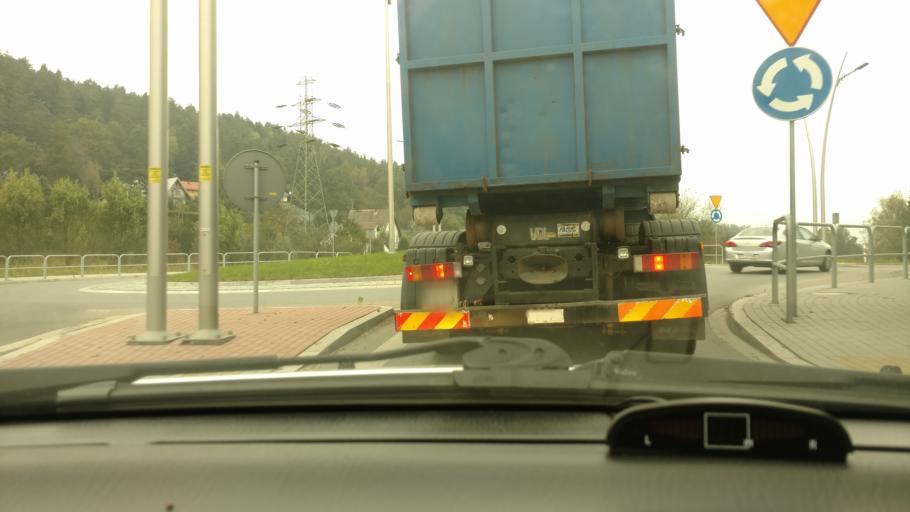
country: PL
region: Lesser Poland Voivodeship
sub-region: Powiat nowosadecki
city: Chelmiec
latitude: 49.6398
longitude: 20.6657
